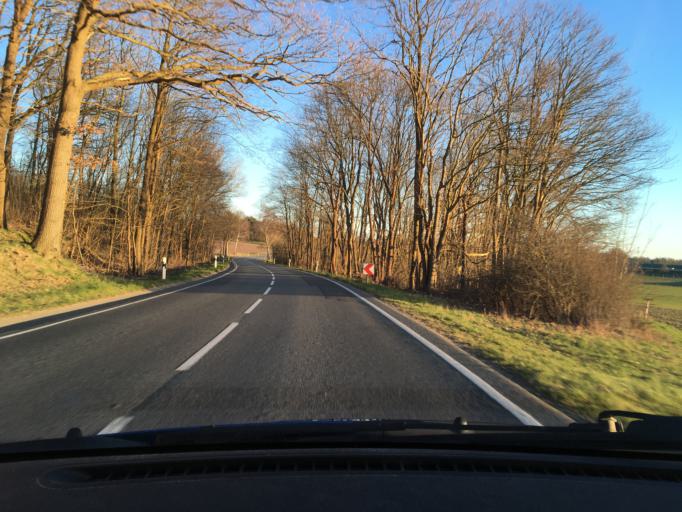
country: DE
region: Lower Saxony
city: Dahlem
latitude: 53.1967
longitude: 10.7513
